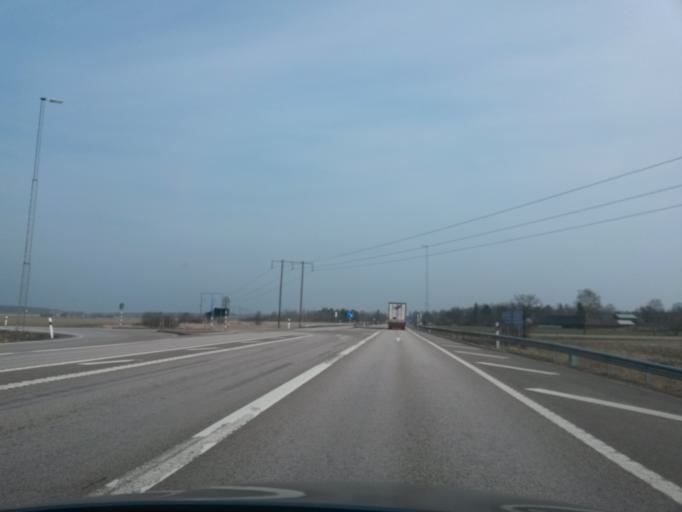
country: SE
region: Vaestra Goetaland
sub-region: Mariestads Kommun
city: Mariestad
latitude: 58.7455
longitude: 13.9479
